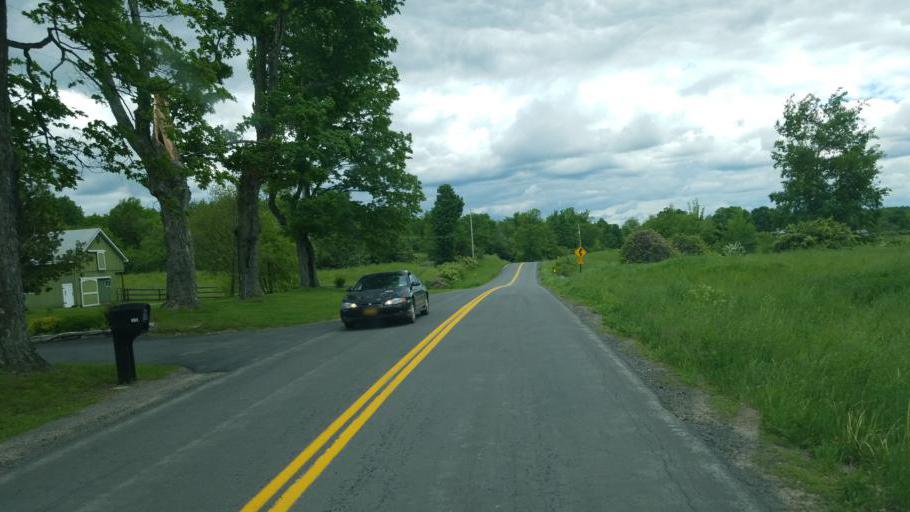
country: US
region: New York
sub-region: Herkimer County
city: Frankfort
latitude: 42.9157
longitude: -75.1433
